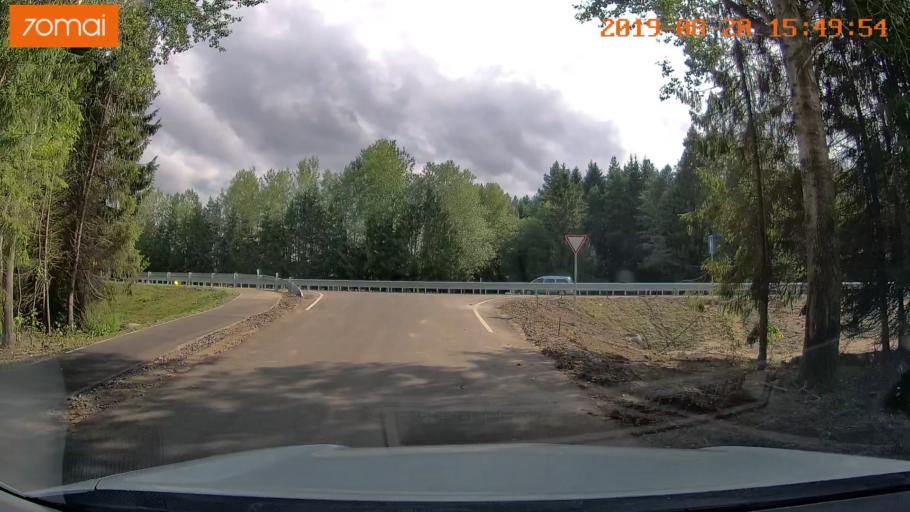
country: BY
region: Minsk
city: Slabada
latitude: 54.0360
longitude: 27.8399
